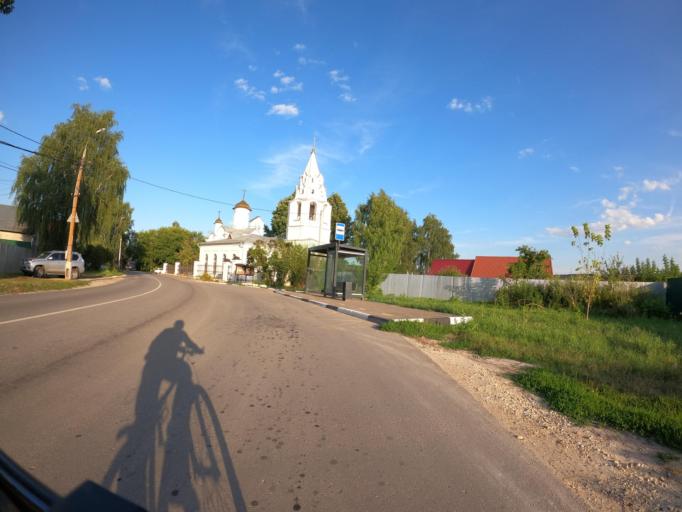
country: RU
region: Moskovskaya
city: Raduzhnyy
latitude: 55.1003
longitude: 38.7248
